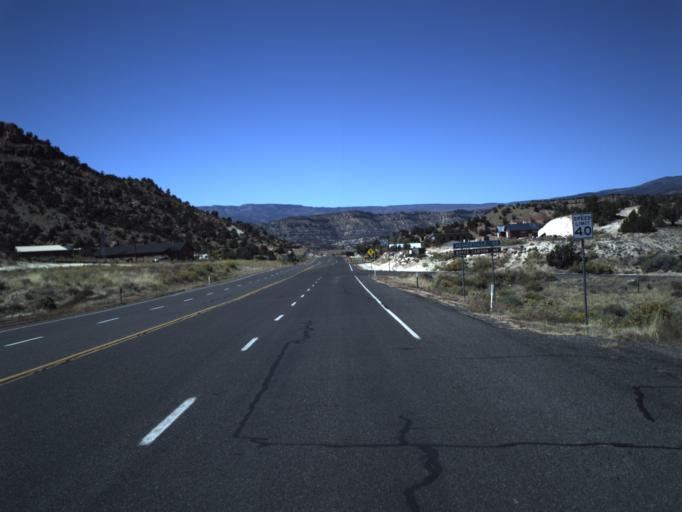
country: US
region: Utah
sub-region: Wayne County
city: Loa
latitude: 37.7717
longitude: -111.6116
